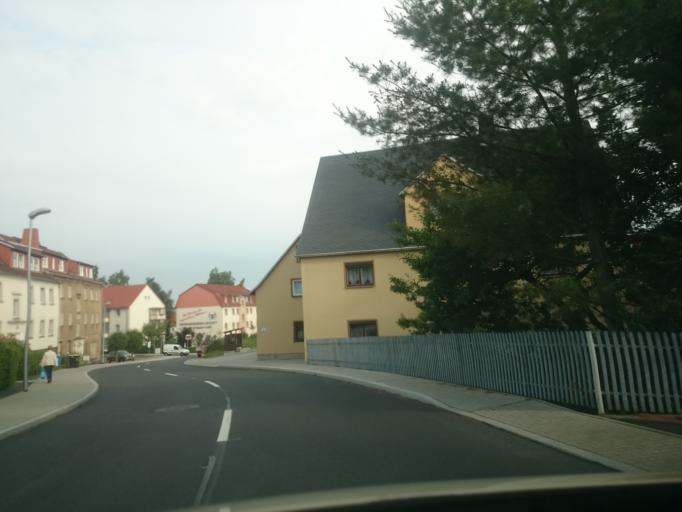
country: DE
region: Saxony
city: Brand-Erbisdorf
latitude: 50.8640
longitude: 13.3188
